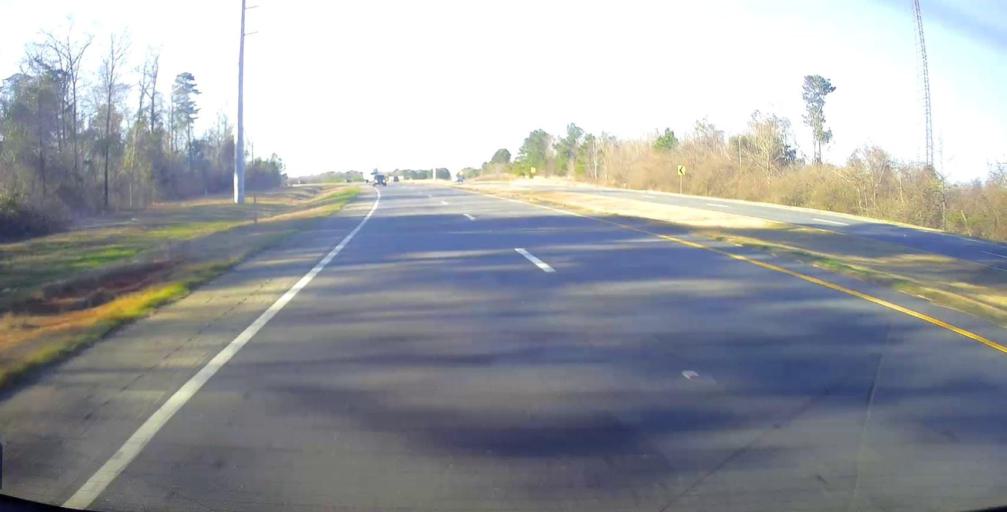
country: US
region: Georgia
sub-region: Lee County
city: Leesburg
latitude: 31.8875
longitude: -84.2460
